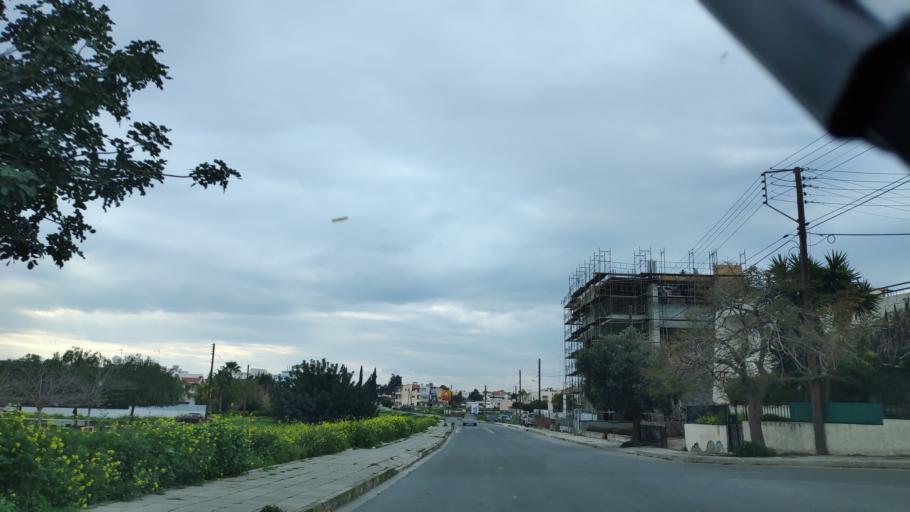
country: CY
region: Limassol
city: Limassol
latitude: 34.6950
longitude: 33.0209
